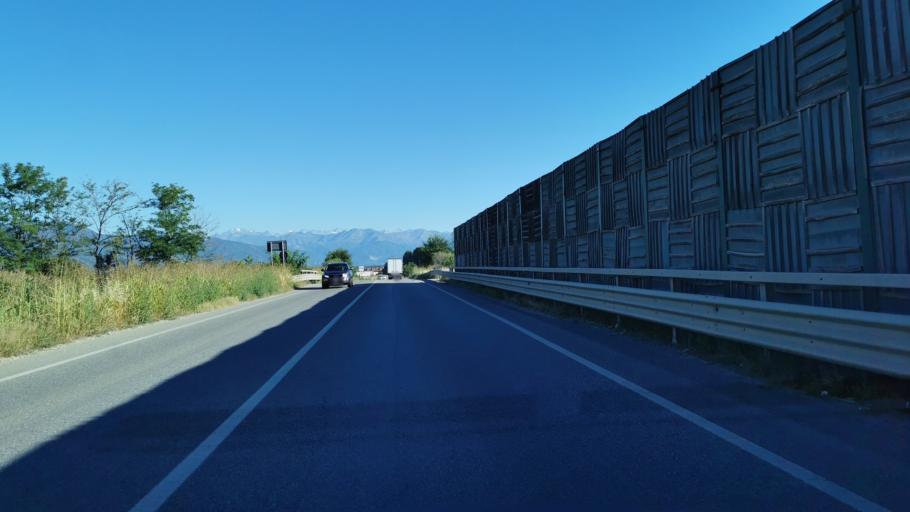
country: IT
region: Piedmont
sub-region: Provincia di Torino
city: Savonera
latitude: 45.1124
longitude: 7.5919
